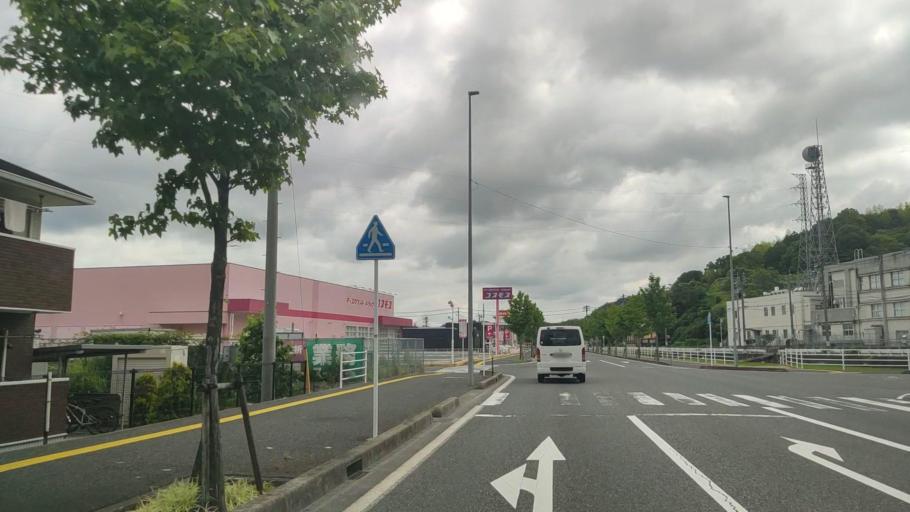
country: JP
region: Tottori
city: Yonago
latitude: 35.4182
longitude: 133.3359
